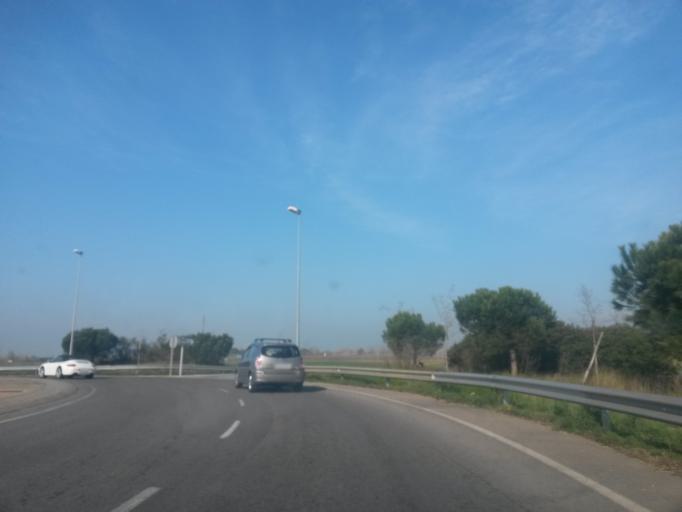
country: ES
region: Catalonia
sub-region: Provincia de Girona
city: Castello d'Empuries
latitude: 42.2575
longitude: 3.0574
